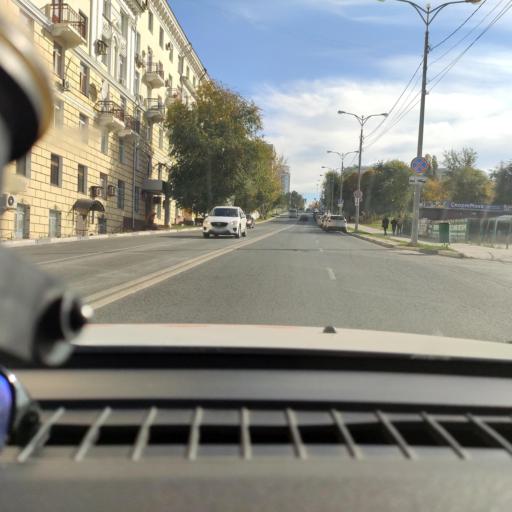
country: RU
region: Samara
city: Samara
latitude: 53.2042
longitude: 50.1101
